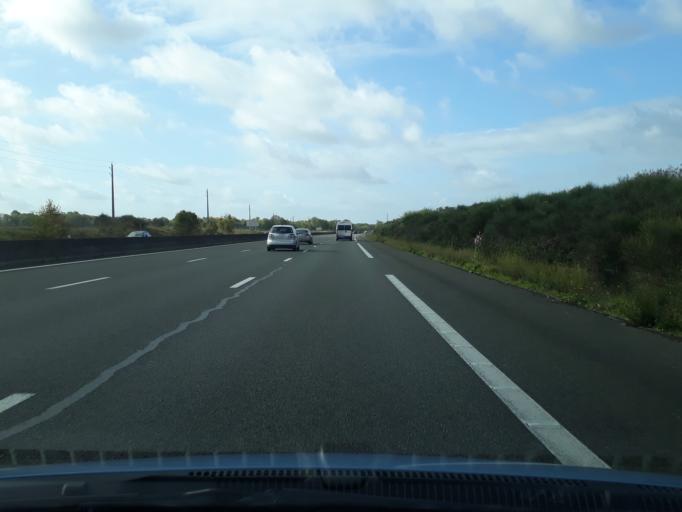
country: FR
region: Centre
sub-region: Departement du Loir-et-Cher
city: Mer
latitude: 47.7412
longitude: 1.5283
